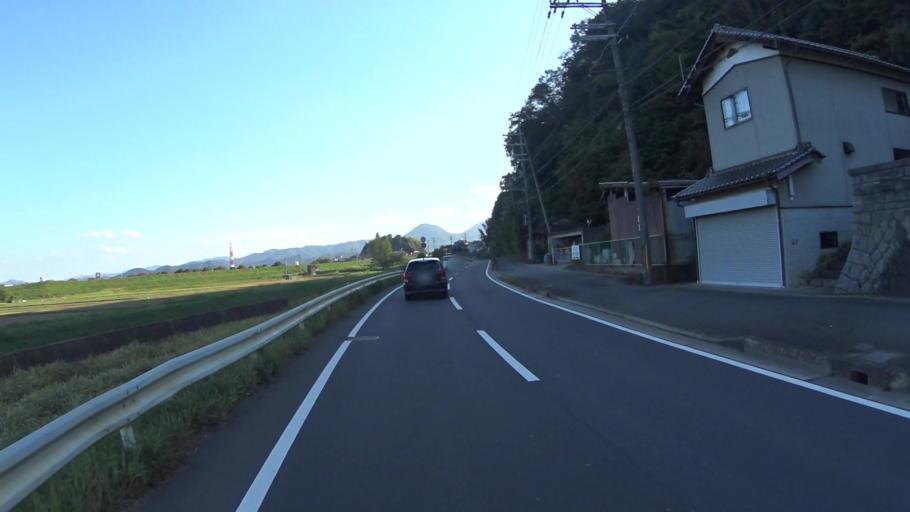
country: JP
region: Kyoto
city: Fukuchiyama
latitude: 35.3177
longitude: 135.1095
